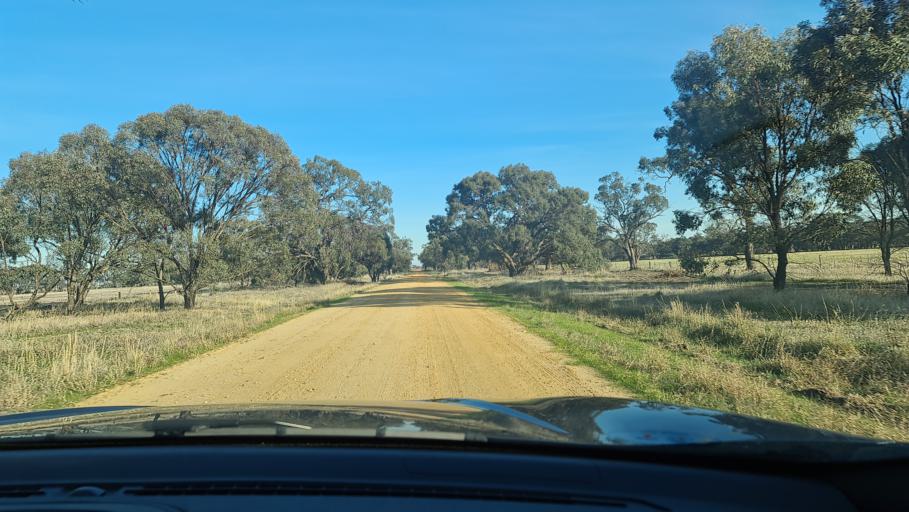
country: AU
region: Victoria
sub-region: Horsham
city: Horsham
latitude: -36.3538
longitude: 142.4008
